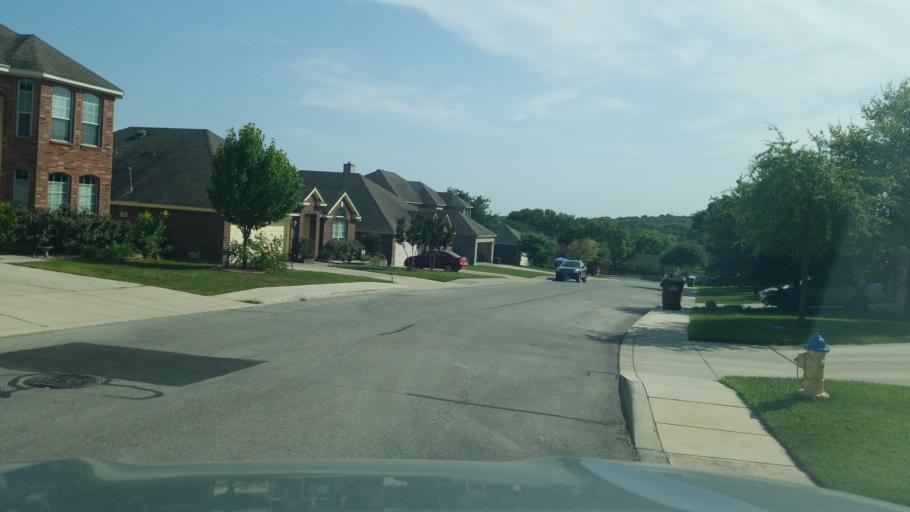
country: US
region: Texas
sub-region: Bexar County
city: Timberwood Park
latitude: 29.6946
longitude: -98.4759
